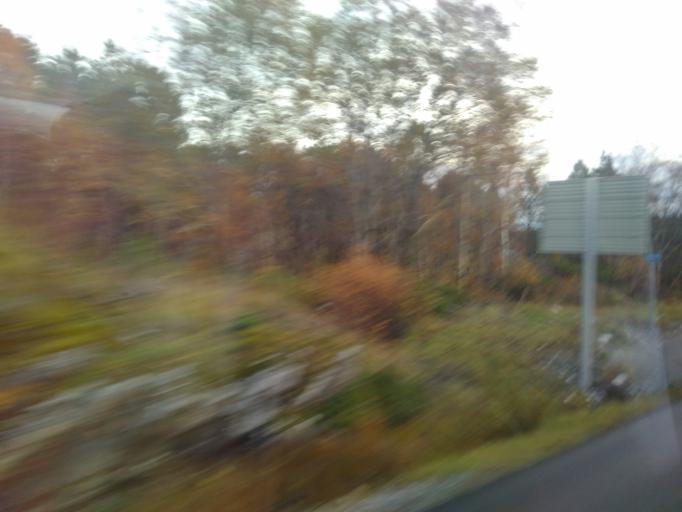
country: NO
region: Sor-Trondelag
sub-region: Froya
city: Sistranda
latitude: 63.6353
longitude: 8.8313
